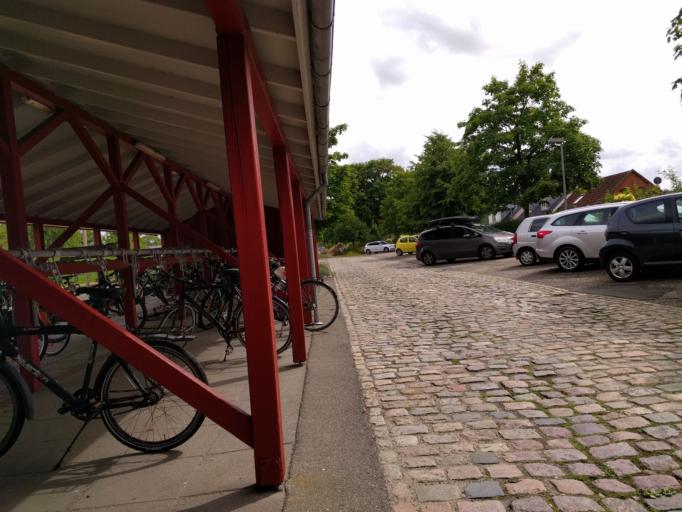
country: DK
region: Central Jutland
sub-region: Skanderborg Kommune
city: Ry
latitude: 56.0907
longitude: 9.7589
